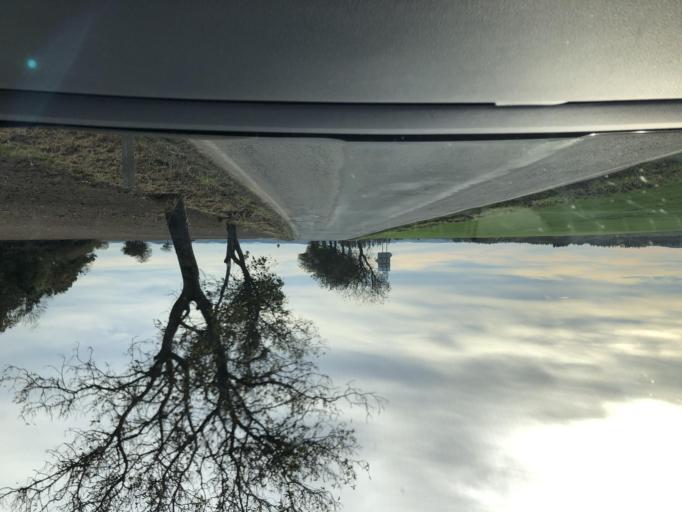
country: CZ
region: Central Bohemia
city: Postupice
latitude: 49.7684
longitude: 14.7816
